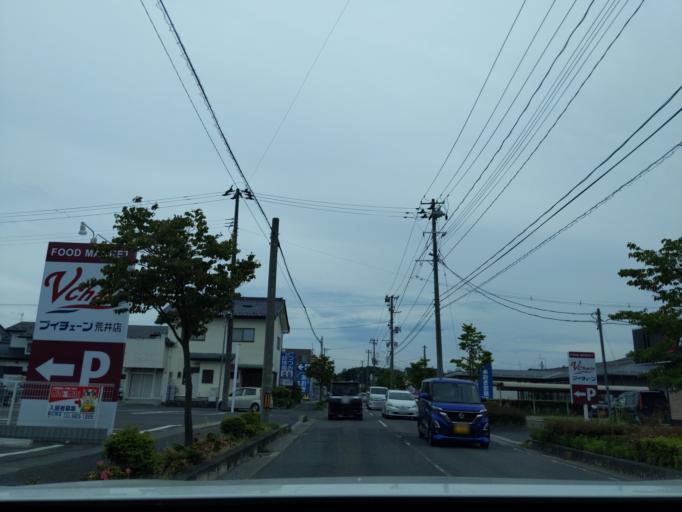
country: JP
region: Fukushima
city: Koriyama
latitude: 37.3716
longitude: 140.3643
